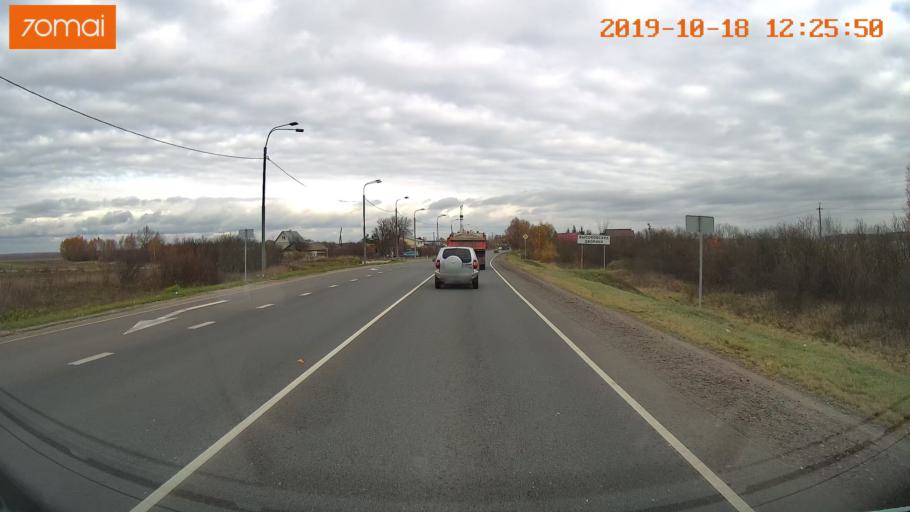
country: RU
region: Rjazan
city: Rybnoye
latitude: 54.5534
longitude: 39.5251
